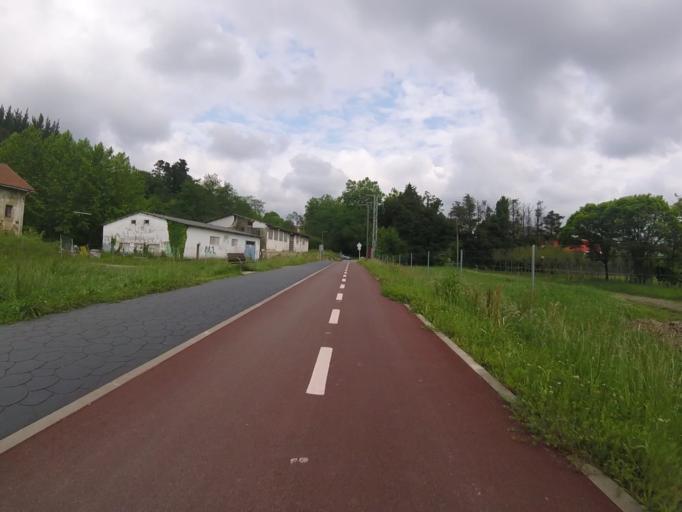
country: ES
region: Basque Country
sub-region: Provincia de Guipuzcoa
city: San Sebastian
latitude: 43.3041
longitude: -1.9565
